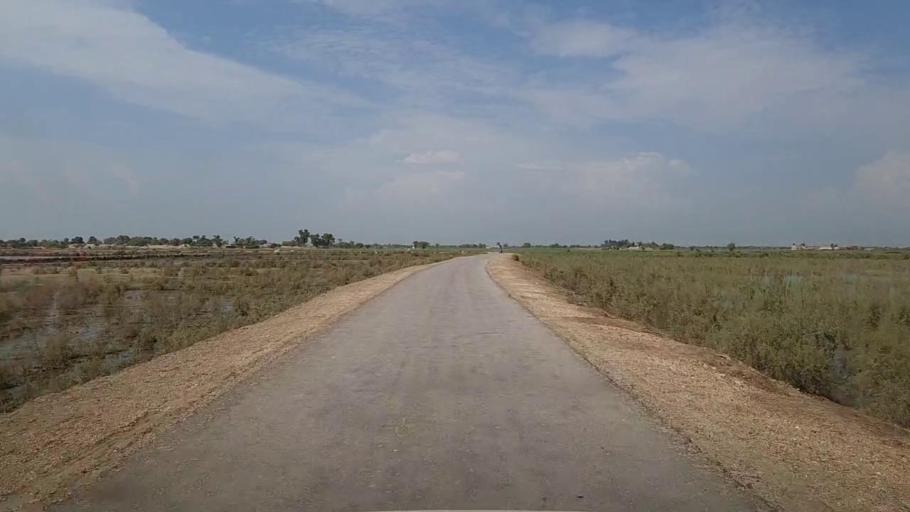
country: PK
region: Sindh
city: Thul
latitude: 28.2870
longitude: 68.8233
